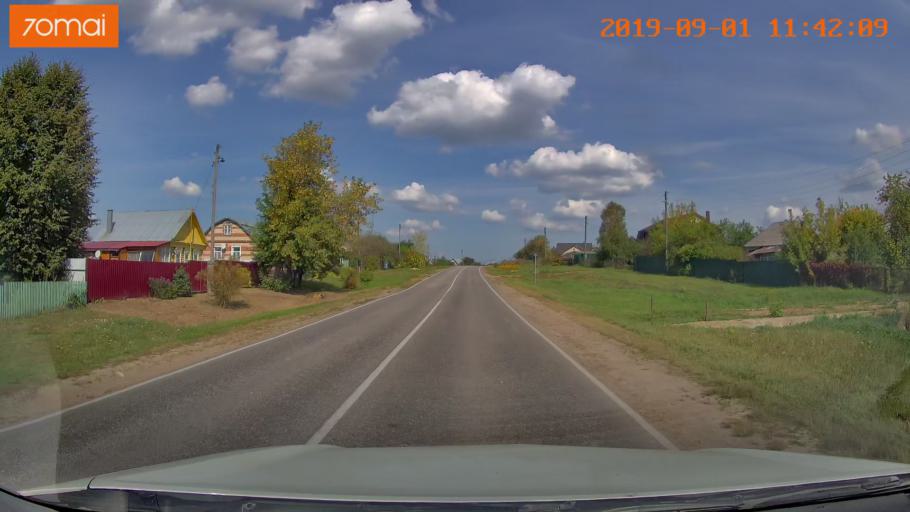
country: RU
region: Kaluga
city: Detchino
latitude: 54.8866
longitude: 36.3788
